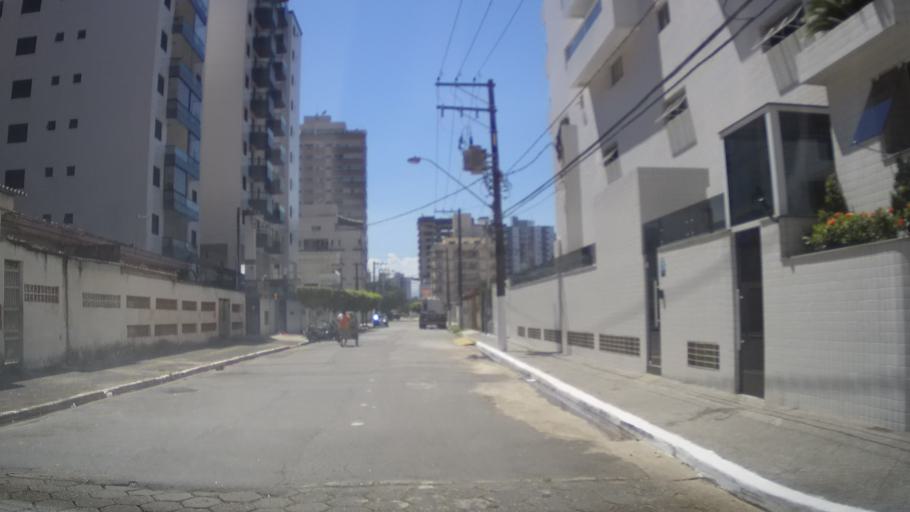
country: BR
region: Sao Paulo
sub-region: Praia Grande
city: Praia Grande
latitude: -24.0269
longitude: -46.4707
